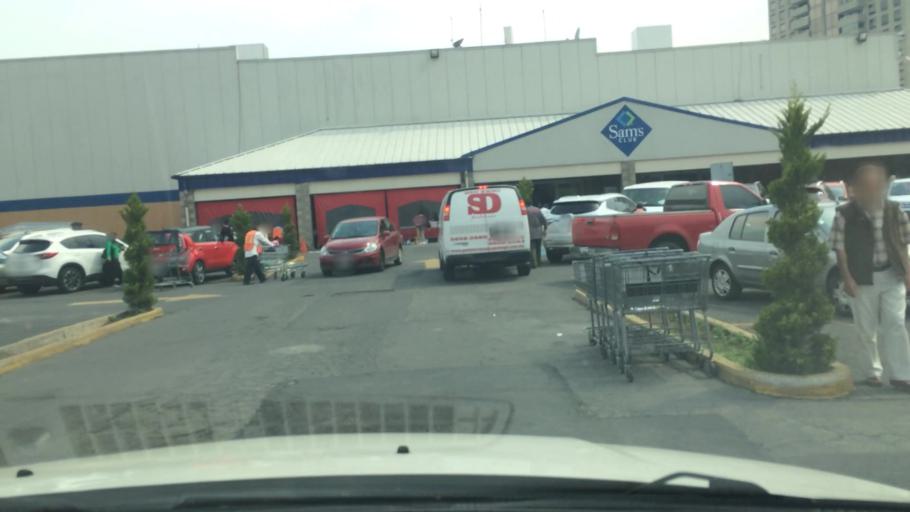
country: MX
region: Mexico City
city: Magdalena Contreras
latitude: 19.3269
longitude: -99.2118
